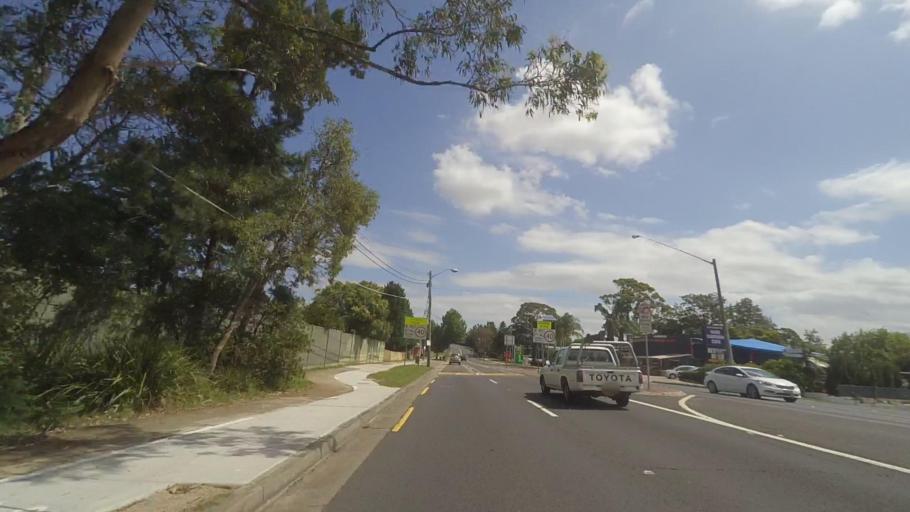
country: AU
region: New South Wales
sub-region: The Hills Shire
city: West Pennant
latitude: -33.7626
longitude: 151.0479
